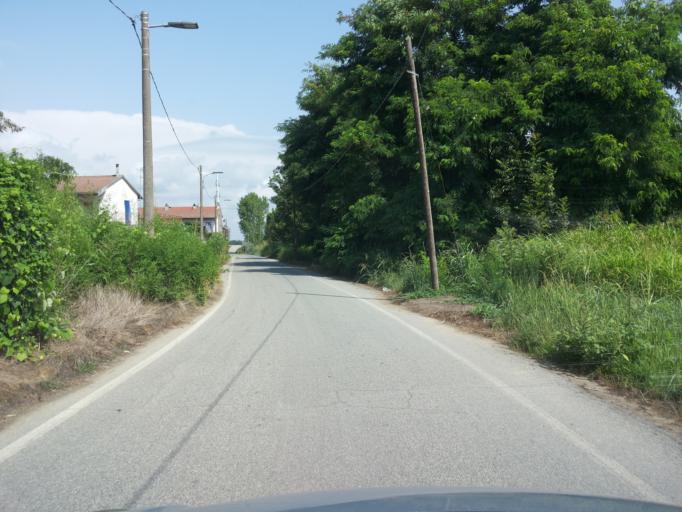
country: IT
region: Lombardy
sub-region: Provincia di Pavia
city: Palestro
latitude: 45.2707
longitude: 8.5370
